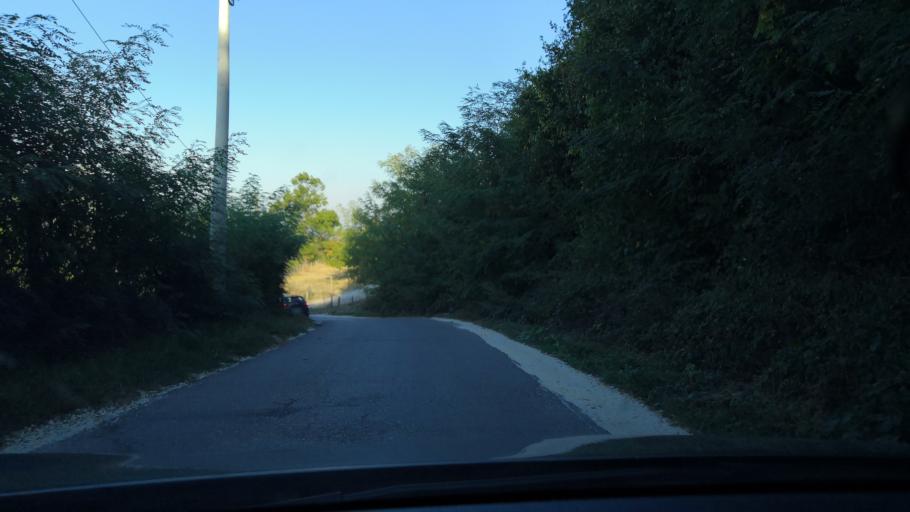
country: RS
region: Central Serbia
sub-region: Sumadijski Okrug
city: Arangelovac
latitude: 44.3320
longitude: 20.5705
